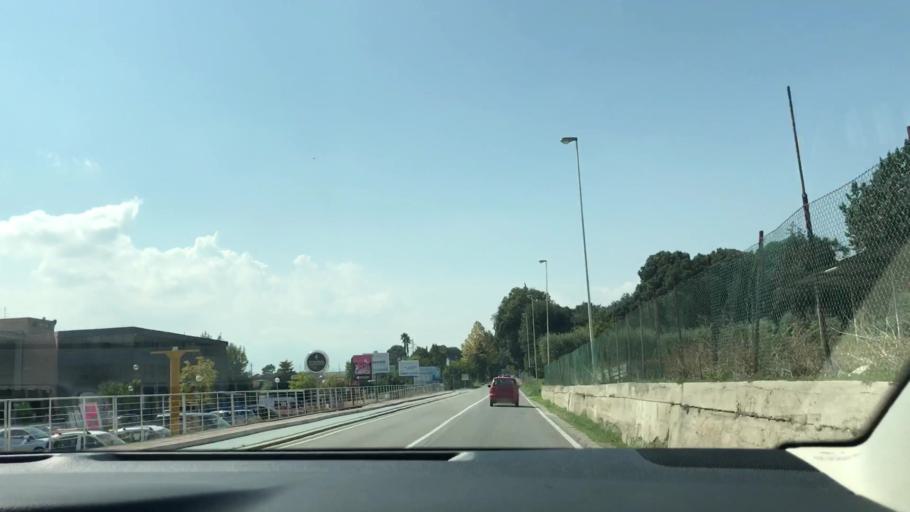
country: IT
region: The Marches
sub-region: Provincia di Ascoli Piceno
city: Centobuchi
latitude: 42.8966
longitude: 13.8458
